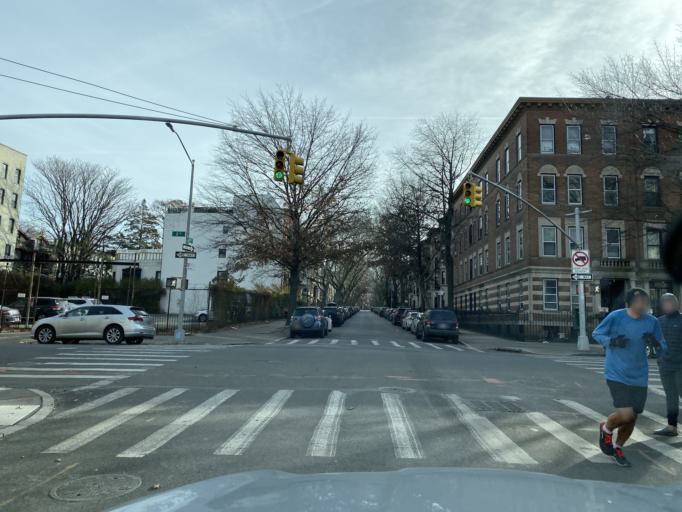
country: US
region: New York
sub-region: Kings County
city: Brooklyn
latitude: 40.6683
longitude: -73.9774
